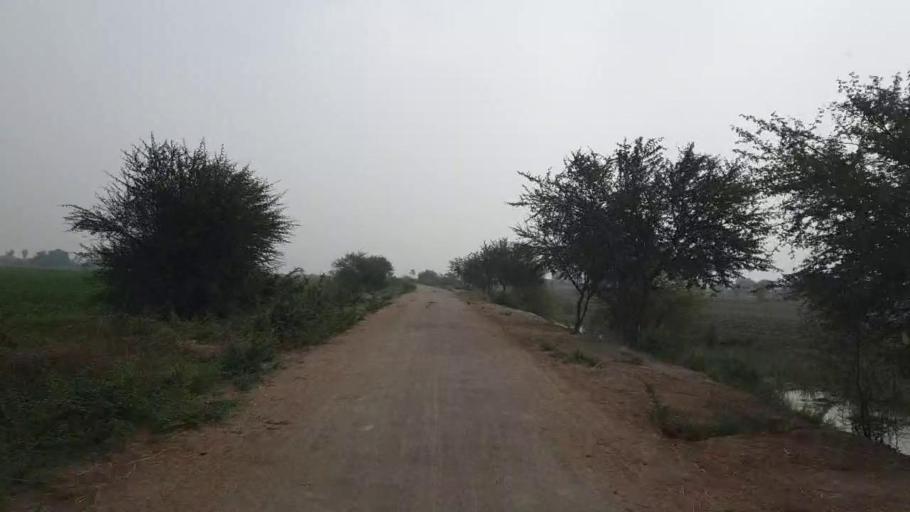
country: PK
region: Sindh
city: Badin
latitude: 24.5745
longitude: 68.6859
